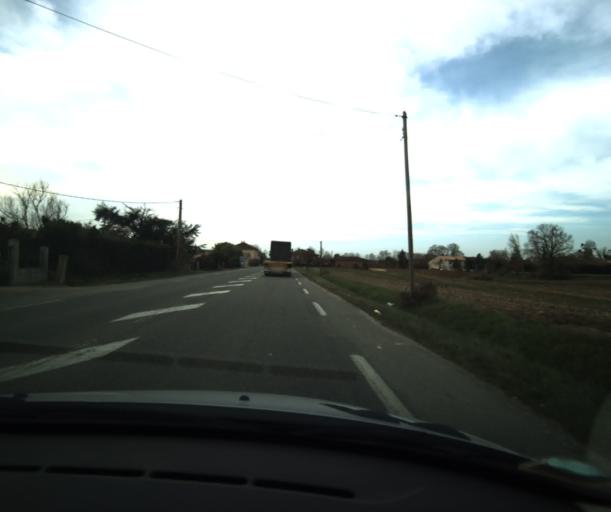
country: FR
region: Midi-Pyrenees
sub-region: Departement du Tarn-et-Garonne
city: Saint-Porquier
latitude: 43.9998
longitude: 1.1841
